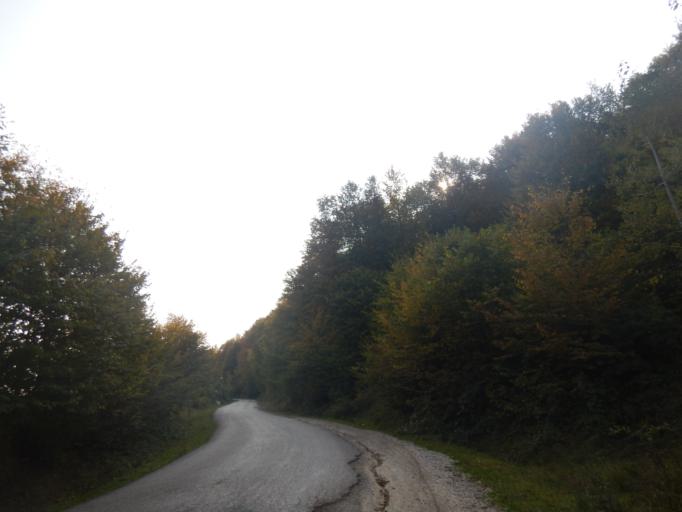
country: TR
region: Ordu
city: Golkoy
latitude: 40.6651
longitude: 37.5580
